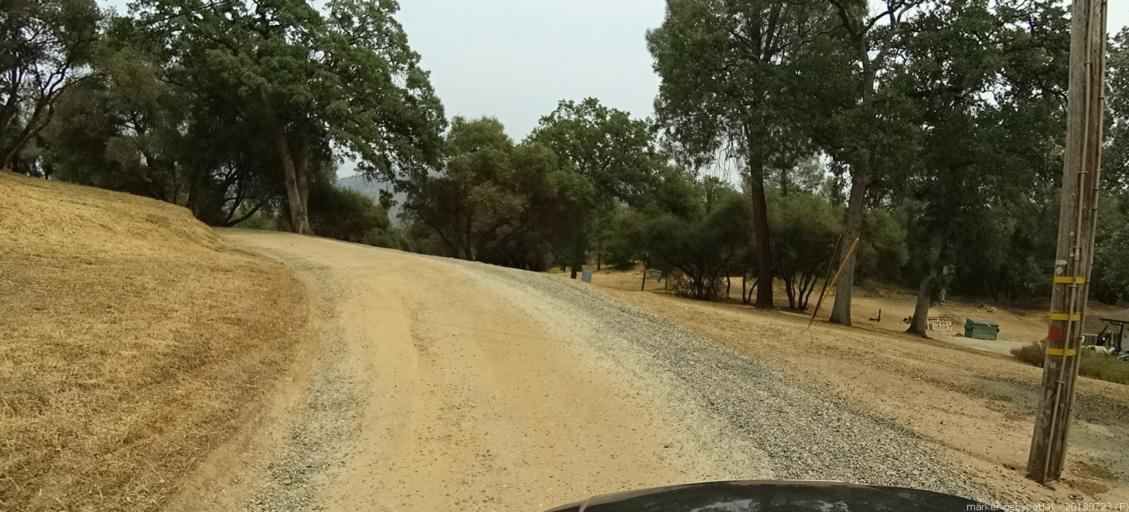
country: US
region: California
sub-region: Madera County
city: Oakhurst
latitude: 37.3434
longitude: -119.6454
